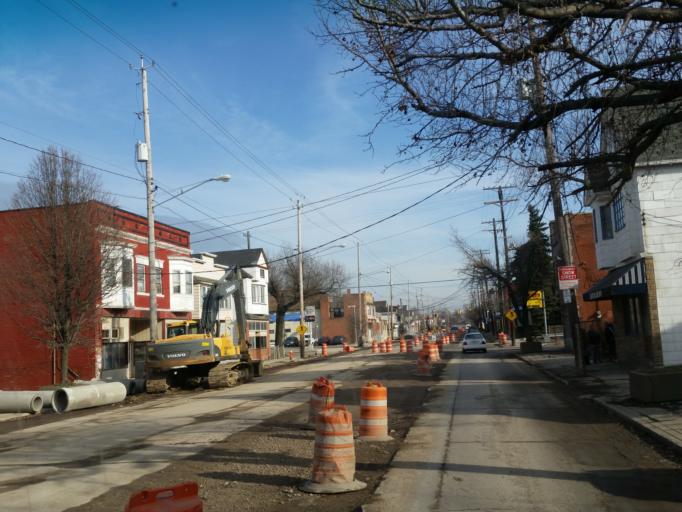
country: US
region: Ohio
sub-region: Cuyahoga County
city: Newburgh Heights
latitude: 41.4559
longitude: -81.6507
